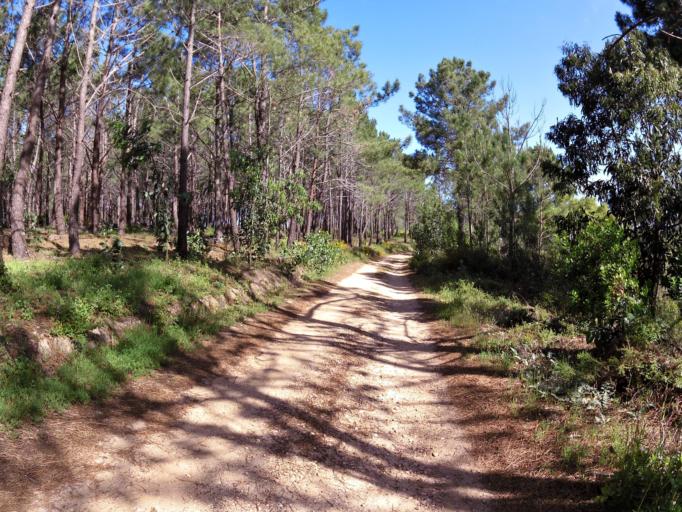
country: PT
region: Faro
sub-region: Aljezur
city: Aljezur
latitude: 37.3324
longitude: -8.8081
